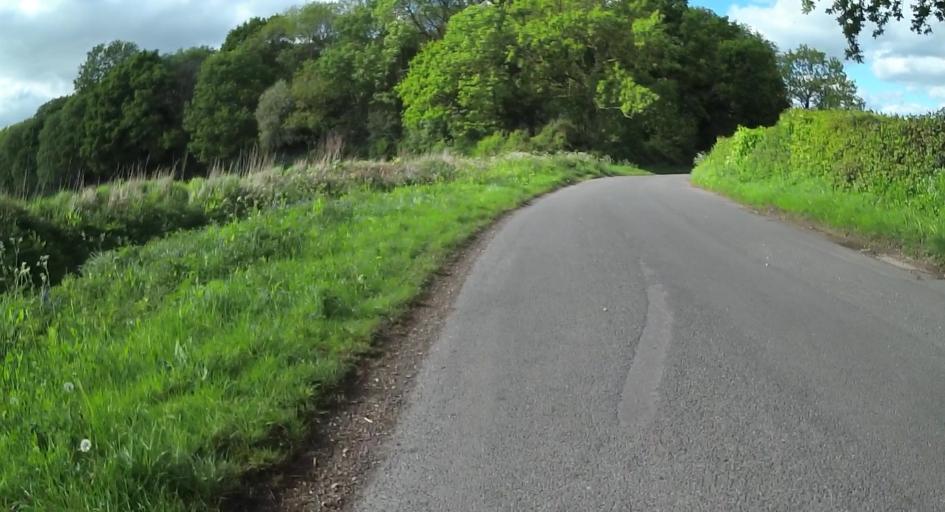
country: GB
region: England
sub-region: West Berkshire
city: Stratfield Mortimer
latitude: 51.3535
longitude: -1.0444
